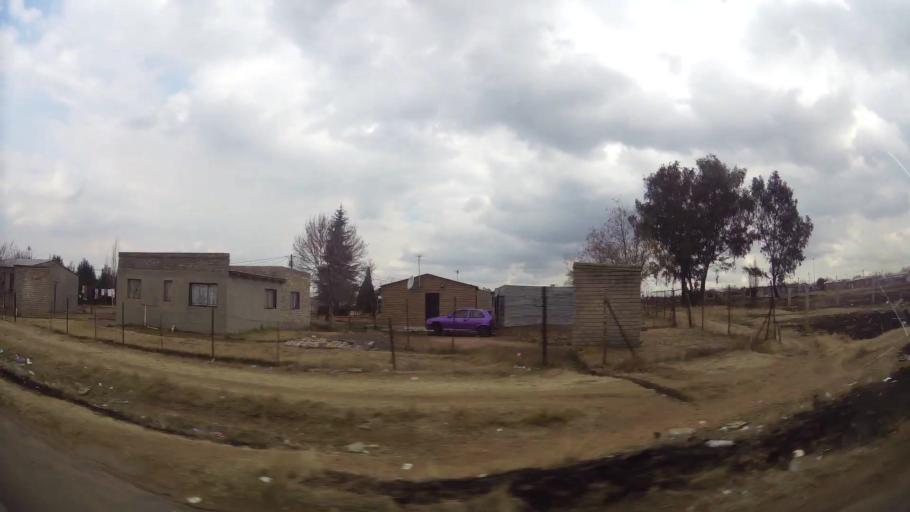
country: ZA
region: Orange Free State
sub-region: Fezile Dabi District Municipality
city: Sasolburg
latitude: -26.8478
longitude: 27.8762
